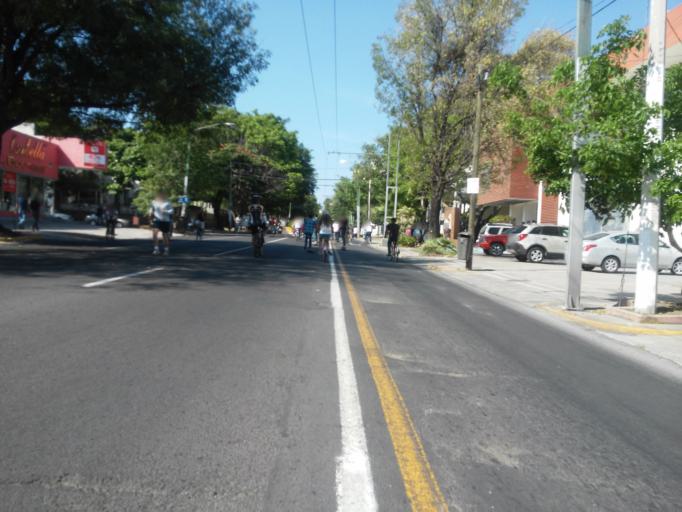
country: MX
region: Jalisco
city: Guadalajara
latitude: 20.6748
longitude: -103.3634
